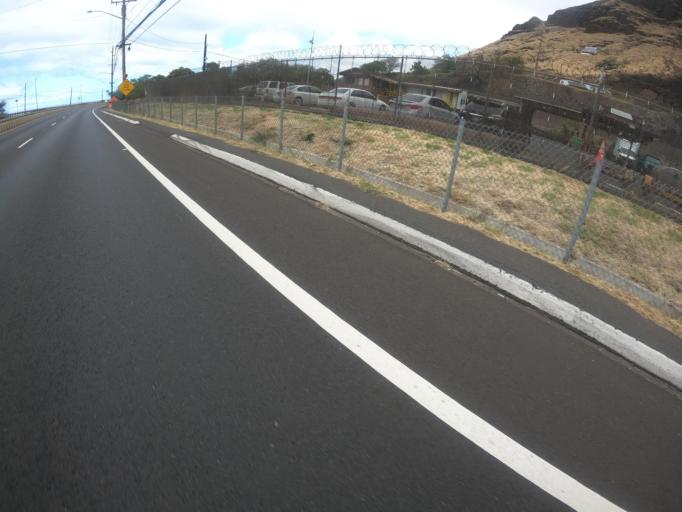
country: US
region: Hawaii
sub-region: Honolulu County
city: Ma'ili
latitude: 21.4011
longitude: -158.1747
